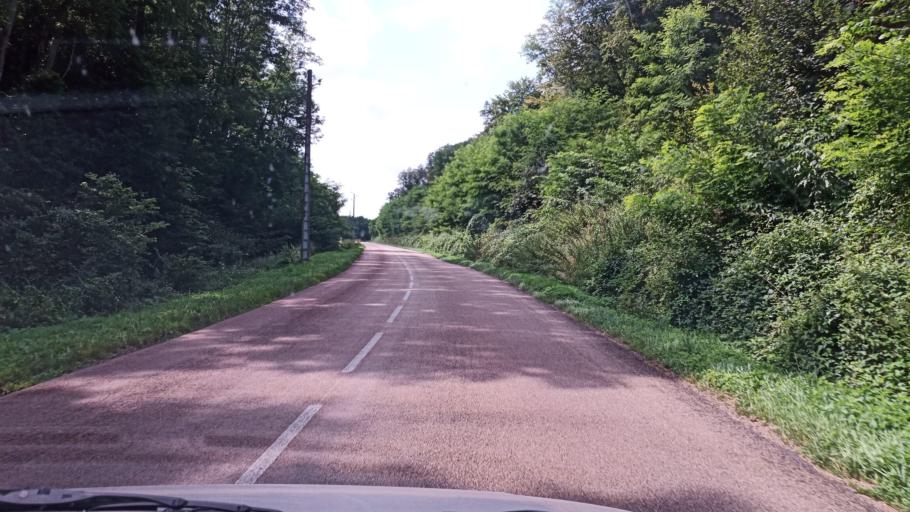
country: FR
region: Bourgogne
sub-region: Departement de l'Yonne
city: Villeneuve-sur-Yonne
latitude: 48.0663
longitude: 3.2619
